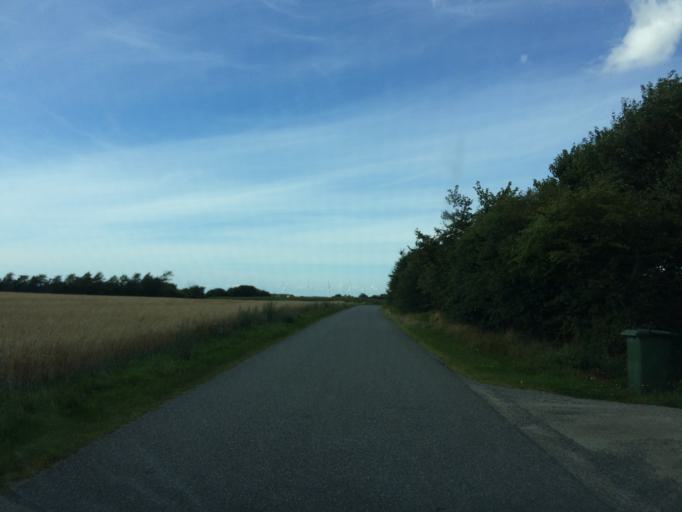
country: DK
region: Central Jutland
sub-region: Ringkobing-Skjern Kommune
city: Skjern
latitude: 56.0180
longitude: 8.4106
